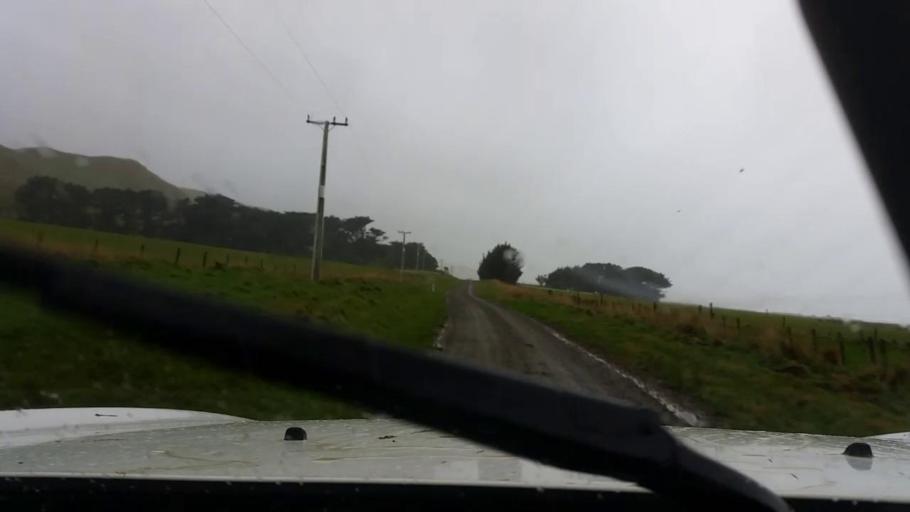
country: NZ
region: Wellington
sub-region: Masterton District
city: Masterton
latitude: -41.2592
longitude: 175.8997
